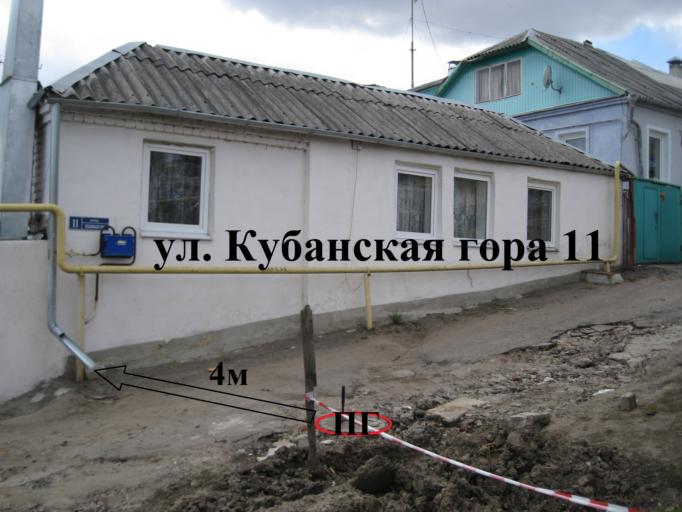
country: RU
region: Voronezj
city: Voronezh
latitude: 51.6393
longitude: 39.2076
